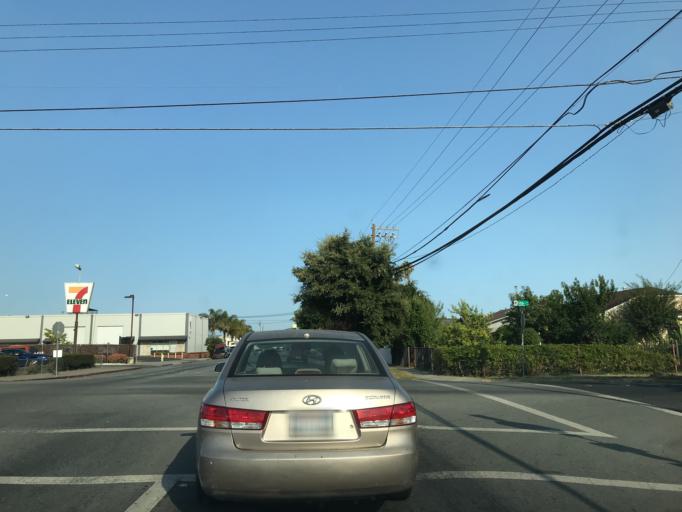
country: US
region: California
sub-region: San Mateo County
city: North Fair Oaks
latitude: 37.4816
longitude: -122.1983
